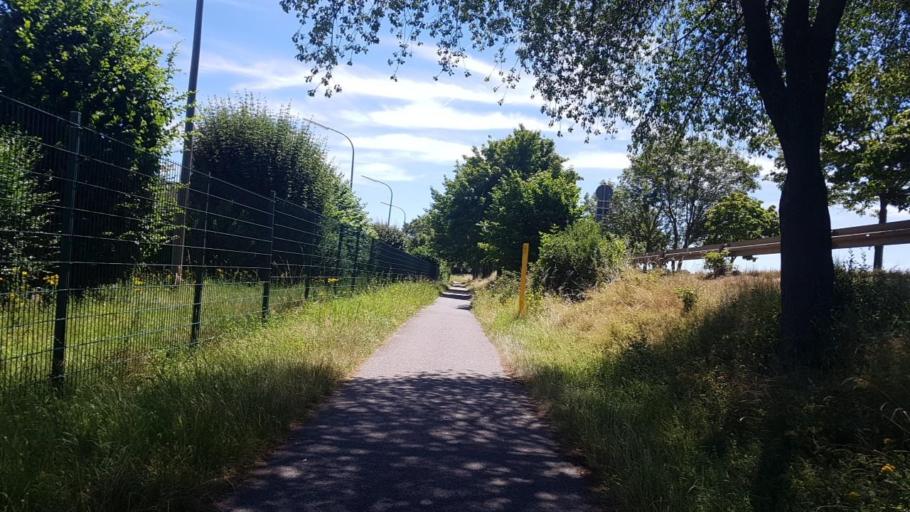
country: DE
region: North Rhine-Westphalia
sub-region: Regierungsbezirk Koln
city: Euskirchen
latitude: 50.6473
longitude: 6.8186
